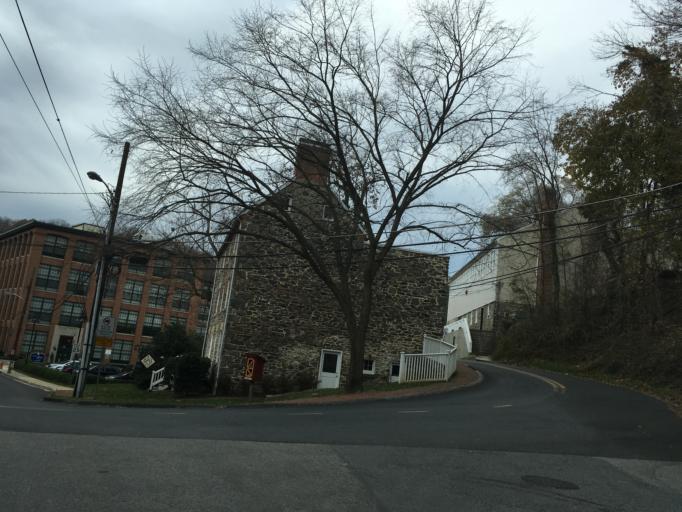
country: US
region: Maryland
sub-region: Howard County
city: Ellicott City
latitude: 39.2741
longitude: -76.7868
